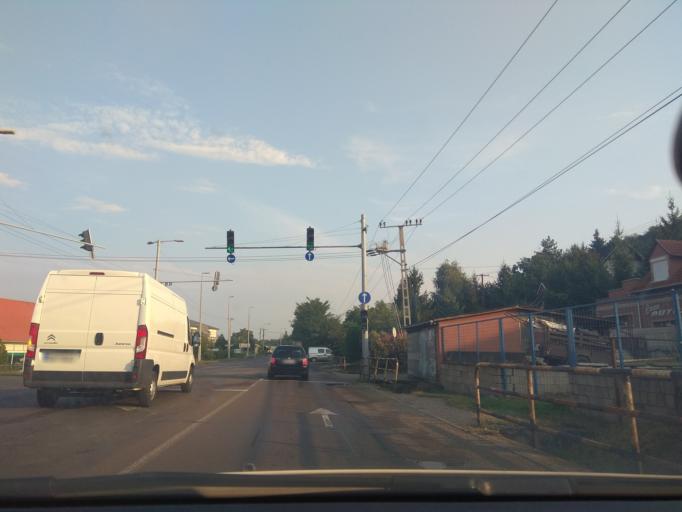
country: HU
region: Heves
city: Andornaktalya
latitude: 47.8726
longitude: 20.4030
